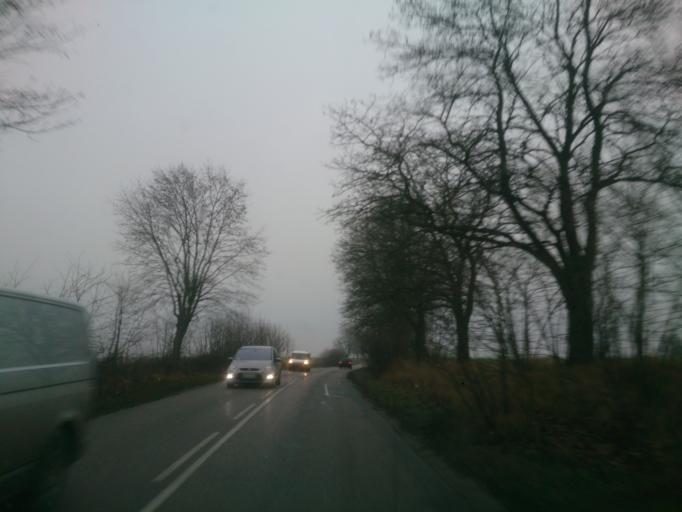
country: PL
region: Pomeranian Voivodeship
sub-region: Powiat koscierski
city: Koscierzyna
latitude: 54.0520
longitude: 18.0420
